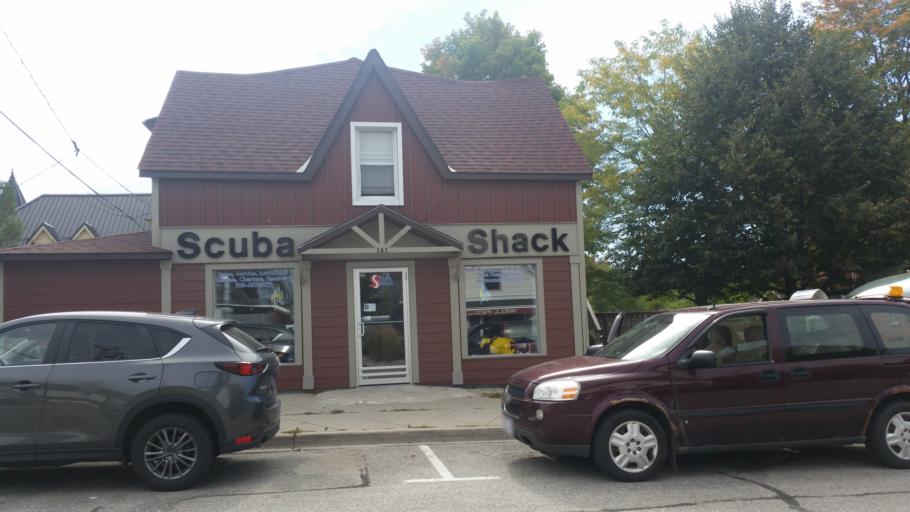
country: CA
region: Ontario
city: Gravenhurst
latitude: 44.9188
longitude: -79.3744
